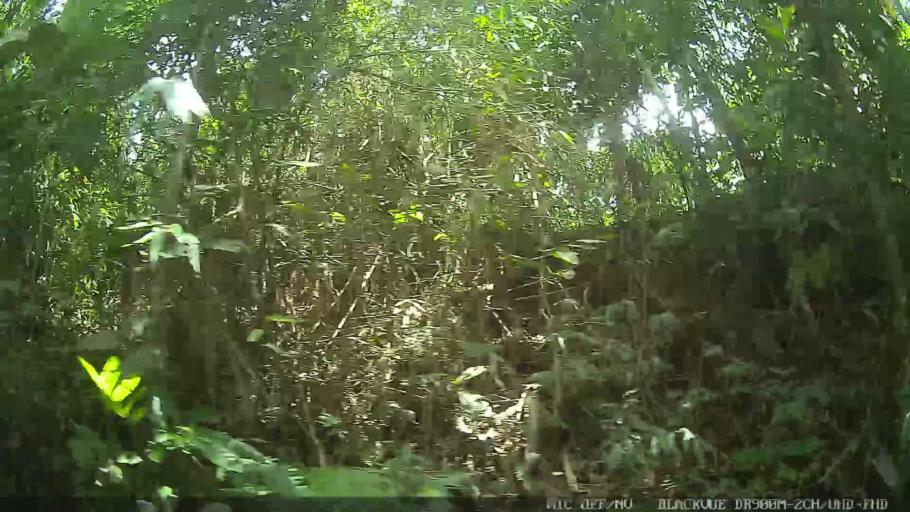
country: BR
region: Sao Paulo
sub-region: Mogi das Cruzes
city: Mogi das Cruzes
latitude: -23.4980
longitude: -46.2026
